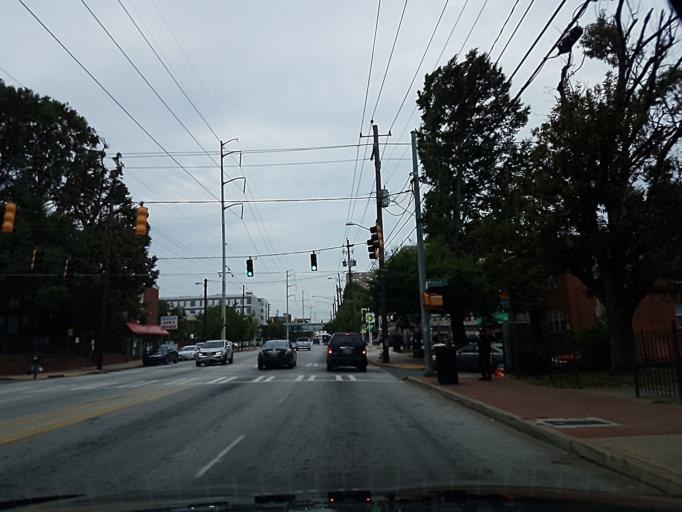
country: US
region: Georgia
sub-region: Fulton County
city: Atlanta
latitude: 33.7651
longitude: -84.3720
